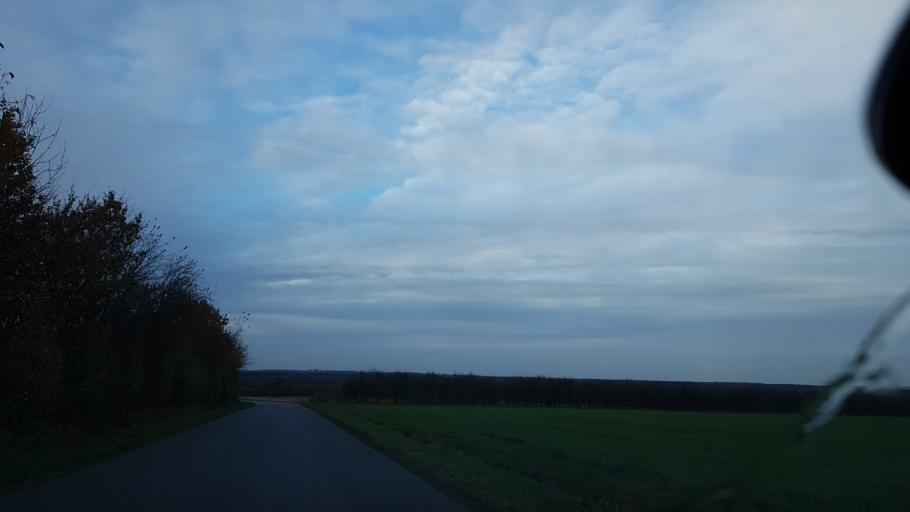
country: DK
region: South Denmark
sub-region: Haderslev Kommune
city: Vojens
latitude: 55.2748
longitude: 9.1933
